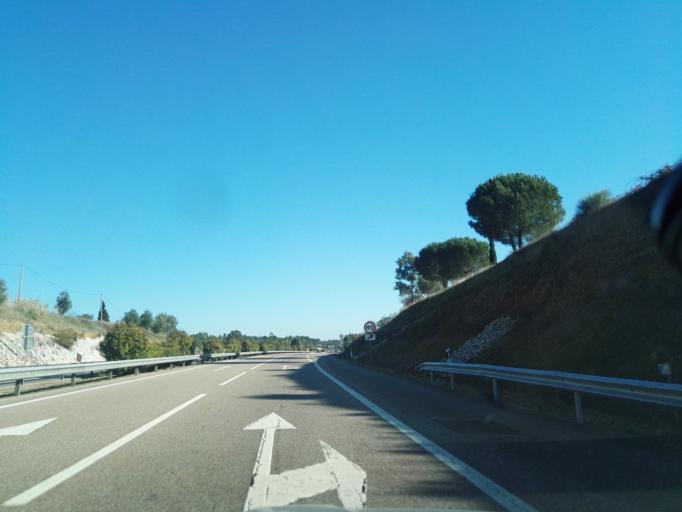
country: PT
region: Santarem
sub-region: Chamusca
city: Vila Nova da Barquinha
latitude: 39.4872
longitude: -8.3944
